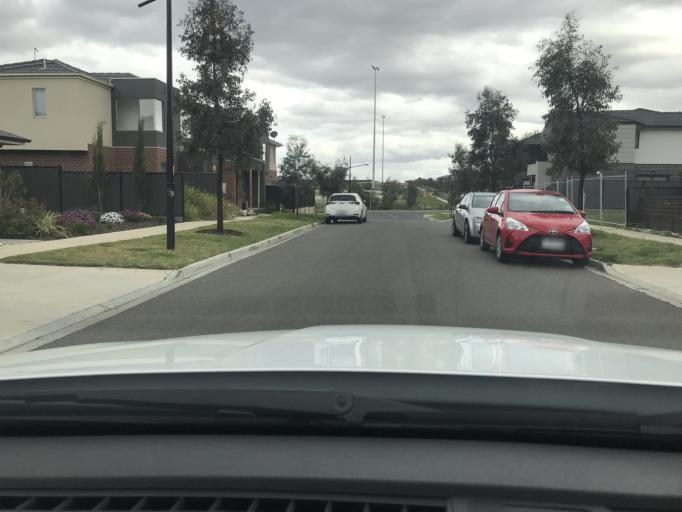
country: AU
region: Victoria
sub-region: Hume
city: Greenvale
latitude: -37.5937
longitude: 144.8907
